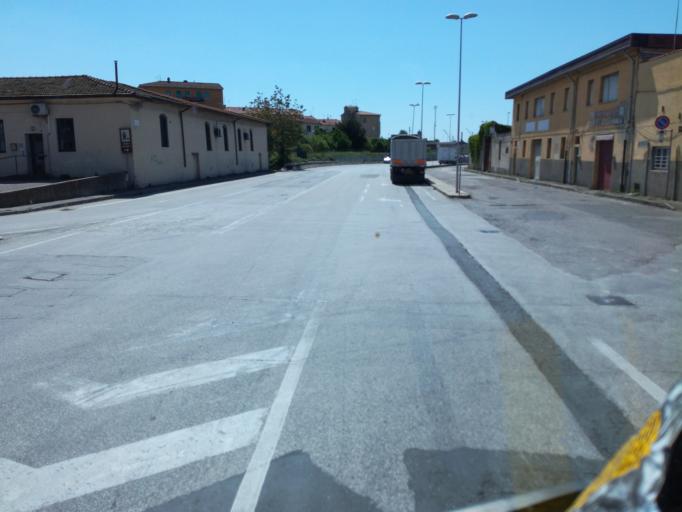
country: IT
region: Tuscany
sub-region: Provincia di Livorno
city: Livorno
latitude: 43.5630
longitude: 10.3123
